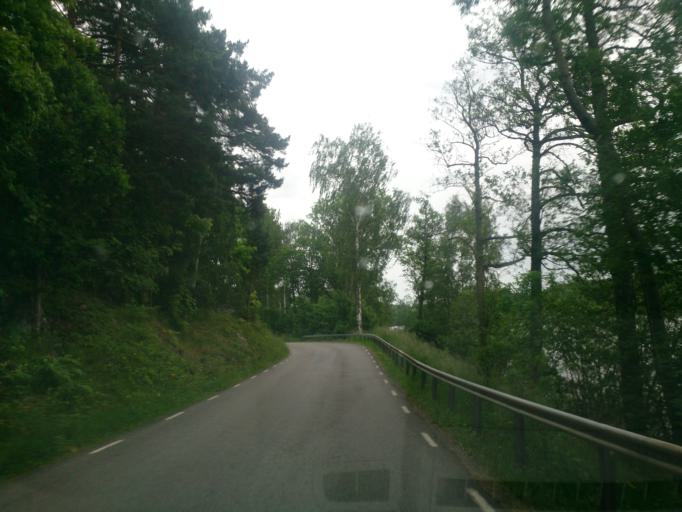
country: SE
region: OEstergoetland
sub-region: Atvidabergs Kommun
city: Atvidaberg
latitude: 58.3141
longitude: 16.0602
